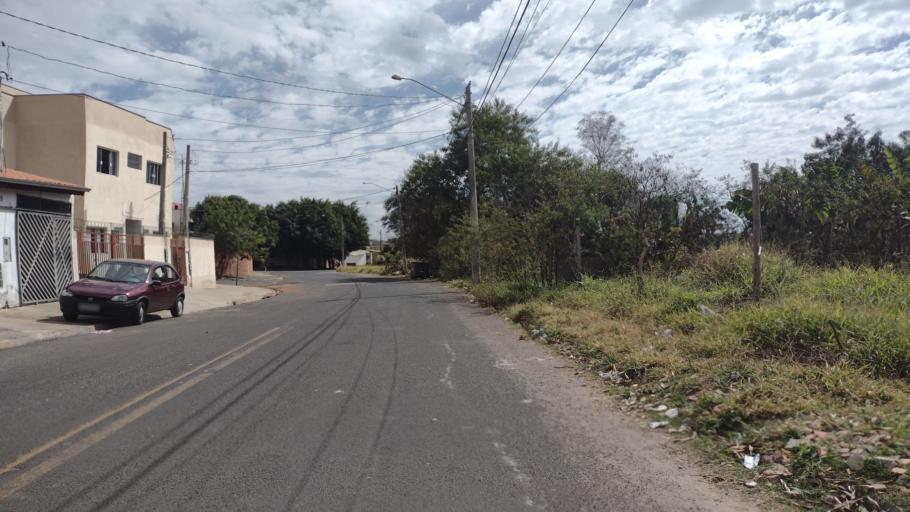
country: BR
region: Sao Paulo
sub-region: Sorocaba
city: Sorocaba
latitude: -23.4244
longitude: -47.4547
